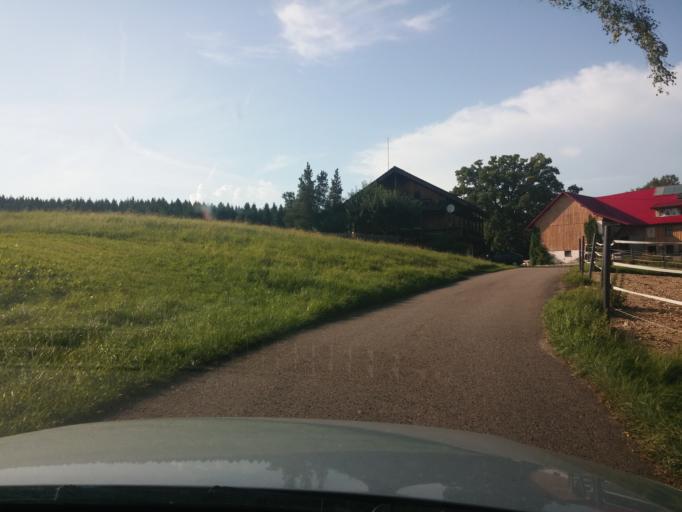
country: DE
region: Bavaria
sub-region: Swabia
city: Lautrach
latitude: 47.8759
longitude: 10.1076
